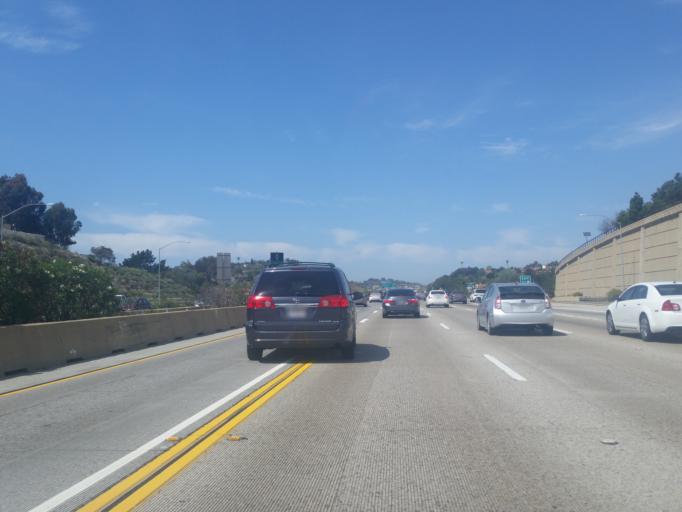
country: US
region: California
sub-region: San Diego County
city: Solana Beach
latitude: 32.9918
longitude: -117.2559
